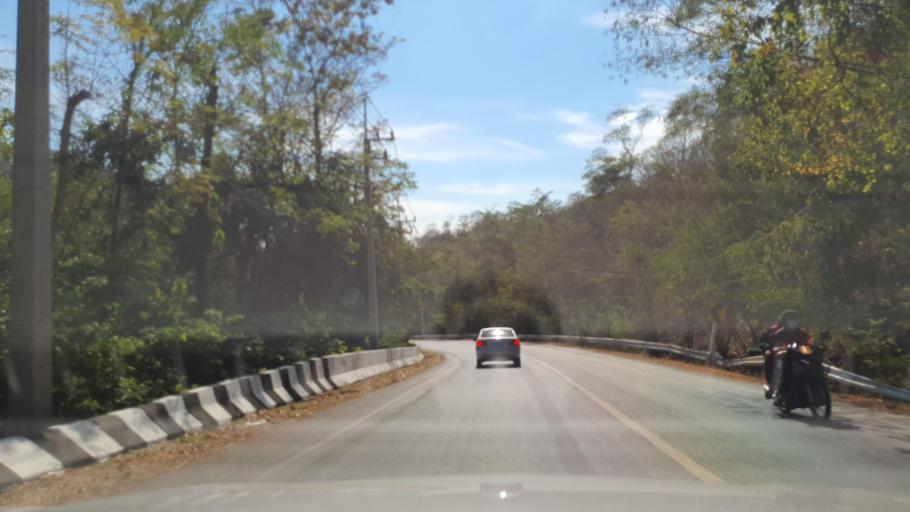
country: TH
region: Kalasin
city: Khao Wong
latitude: 16.7601
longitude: 104.1290
